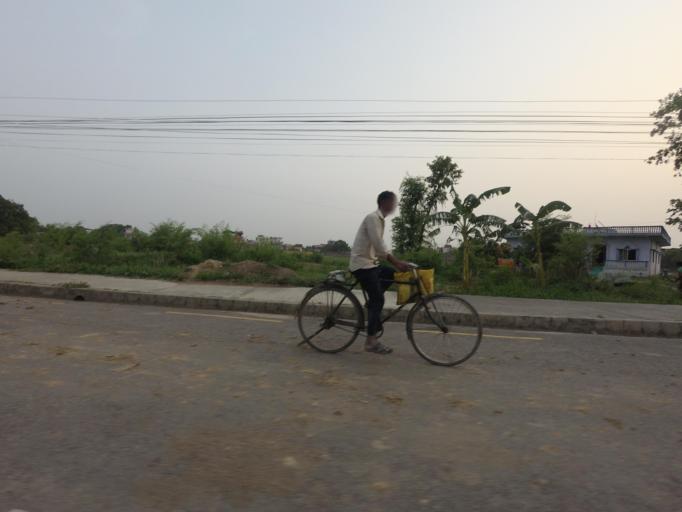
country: NP
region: Western Region
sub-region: Lumbini Zone
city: Bhairahawa
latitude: 27.4962
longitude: 83.4617
